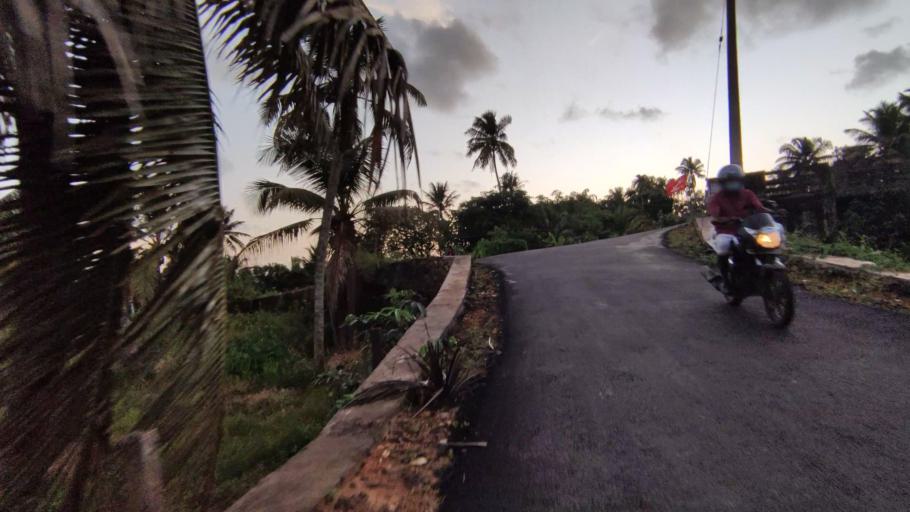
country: IN
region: Kerala
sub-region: Kottayam
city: Kottayam
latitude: 9.5888
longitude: 76.4484
